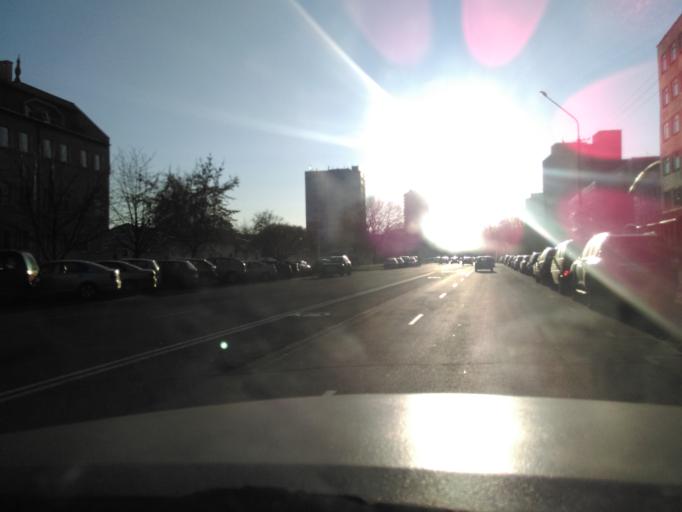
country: BY
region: Minsk
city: Minsk
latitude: 53.9126
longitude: 27.5989
